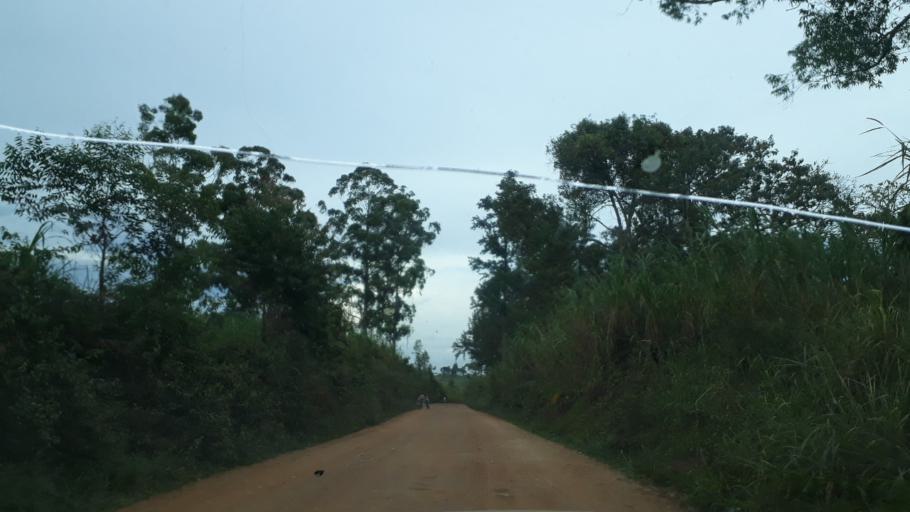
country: CD
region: Eastern Province
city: Bunia
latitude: 1.9226
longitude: 30.5071
